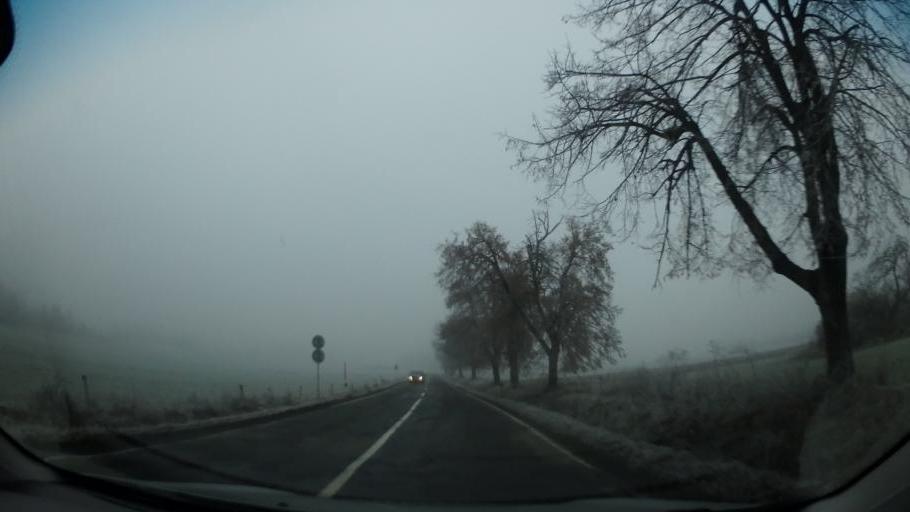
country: CZ
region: Vysocina
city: Budisov
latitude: 49.2719
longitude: 15.9423
